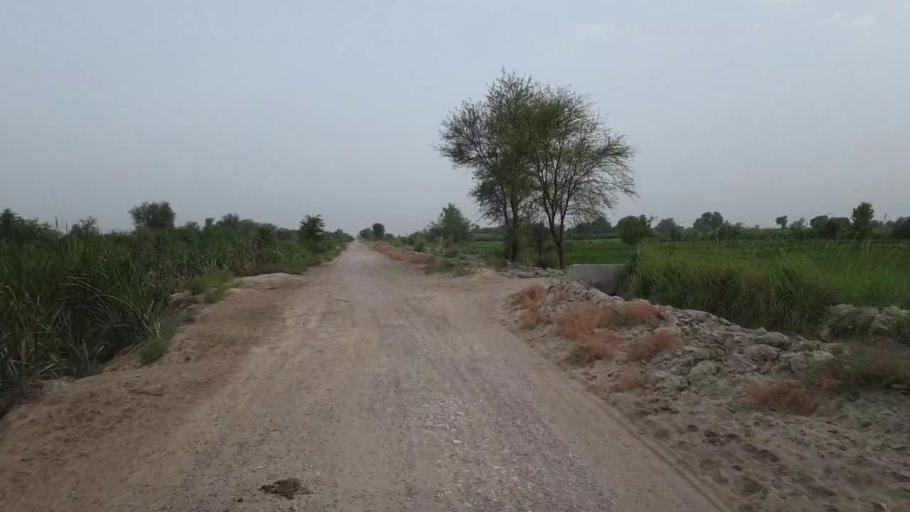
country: PK
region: Sindh
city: Daur
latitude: 26.4204
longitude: 68.2251
